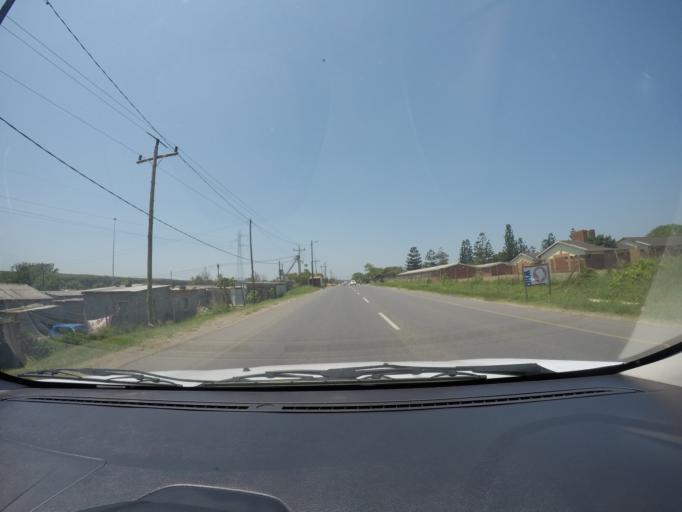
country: ZA
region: KwaZulu-Natal
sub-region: uThungulu District Municipality
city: eSikhawini
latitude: -28.8769
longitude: 31.8940
